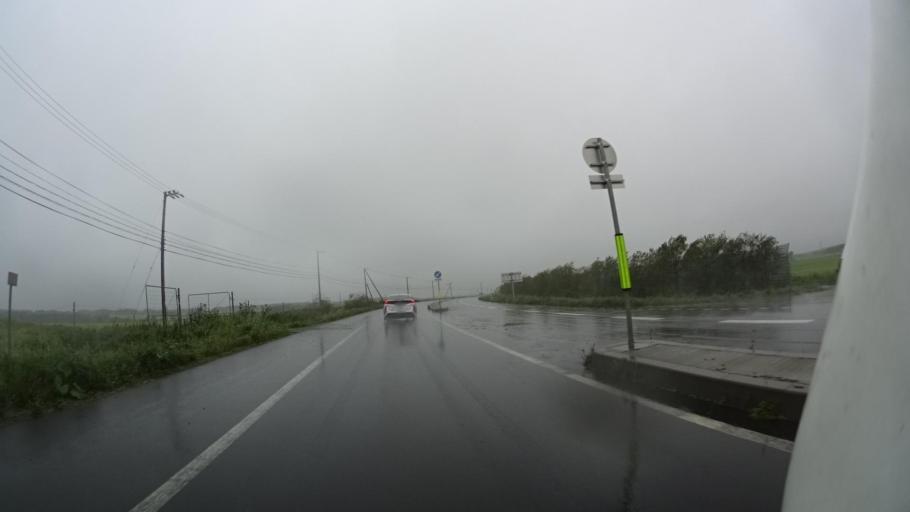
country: JP
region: Hokkaido
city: Nemuro
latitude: 43.2466
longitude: 145.3198
